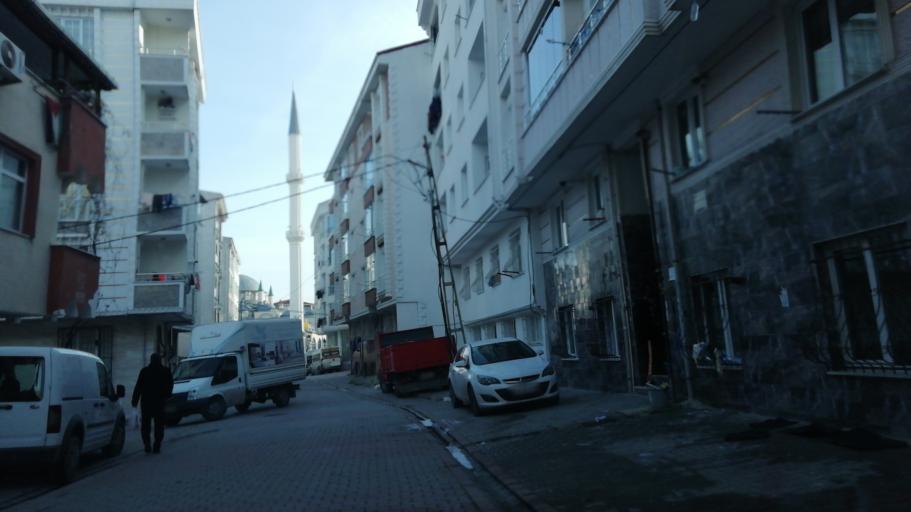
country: TR
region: Istanbul
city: Esenyurt
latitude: 41.0374
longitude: 28.6809
